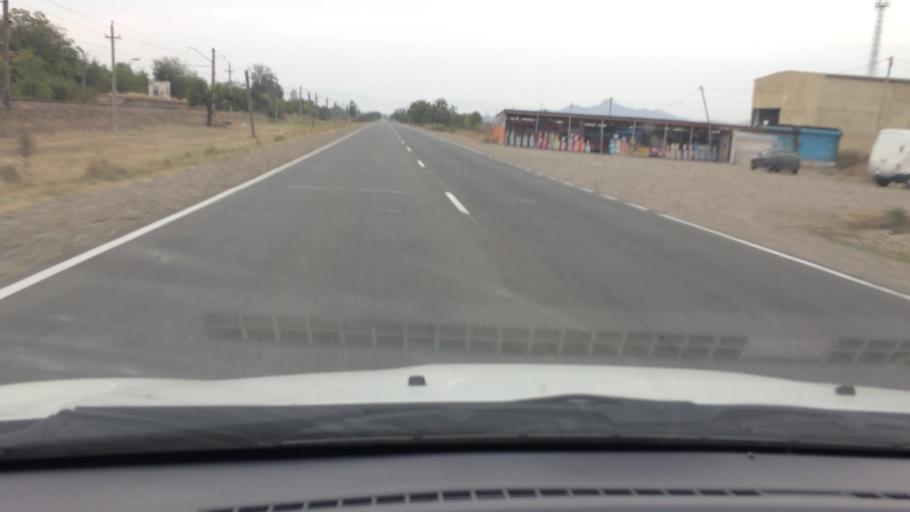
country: GE
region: Kvemo Kartli
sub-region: Marneuli
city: Marneuli
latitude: 41.4359
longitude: 44.8193
